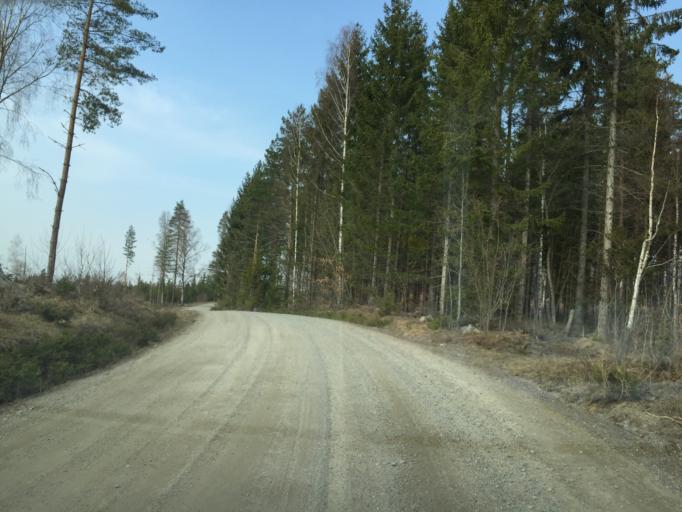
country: SE
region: Soedermanland
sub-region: Vingakers Kommun
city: Vingaker
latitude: 59.0097
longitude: 15.7835
